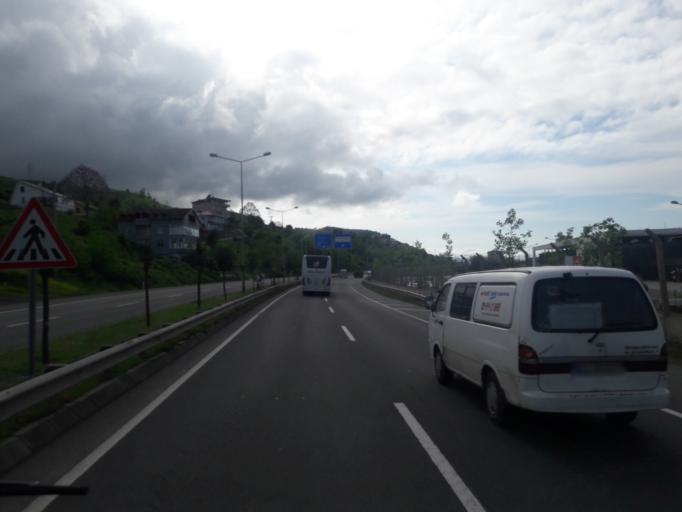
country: TR
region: Ordu
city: Gulyali
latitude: 40.9628
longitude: 38.0819
